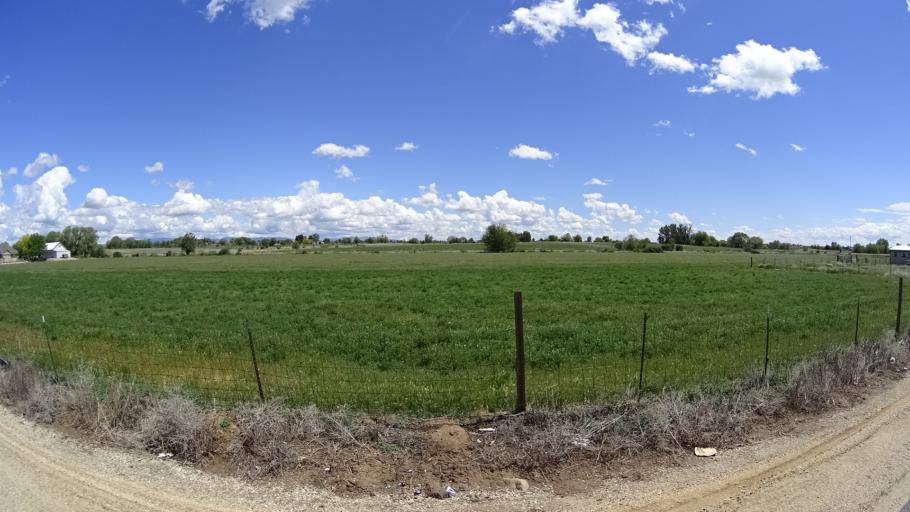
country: US
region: Idaho
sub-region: Ada County
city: Kuna
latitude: 43.5638
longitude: -116.4736
